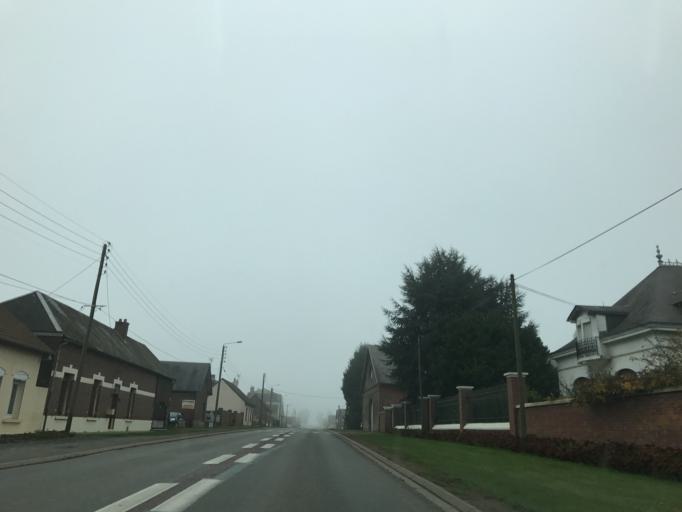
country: FR
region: Nord-Pas-de-Calais
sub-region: Departement du Pas-de-Calais
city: Bapaume
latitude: 50.0602
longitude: 2.8957
